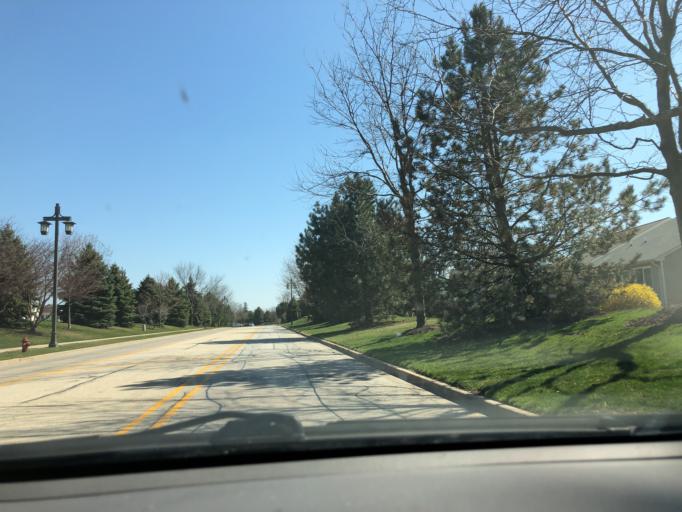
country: US
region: Illinois
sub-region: McHenry County
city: Huntley
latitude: 42.1591
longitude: -88.4565
